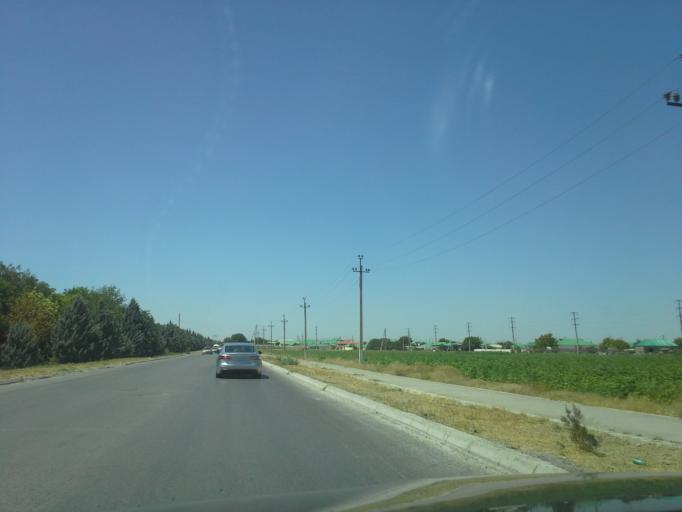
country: TM
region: Ahal
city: Abadan
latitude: 38.0307
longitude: 58.2316
